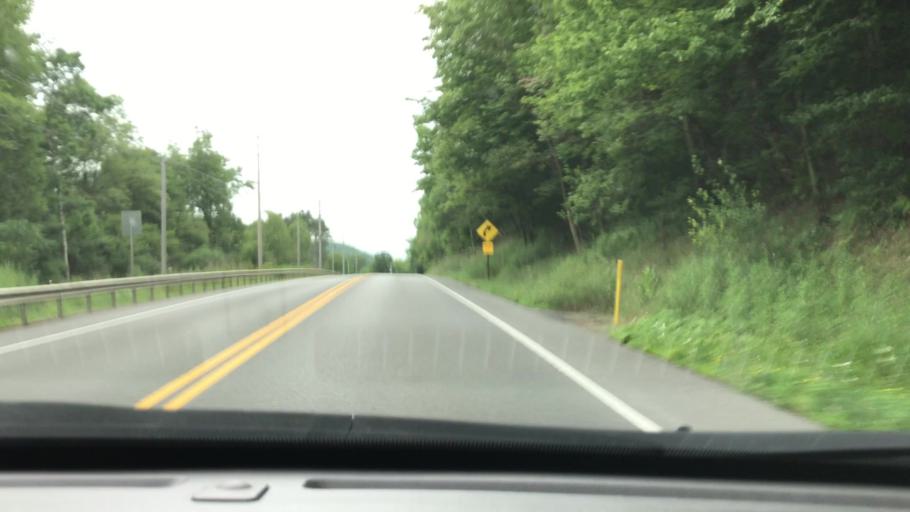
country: US
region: Pennsylvania
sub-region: Elk County
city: Johnsonburg
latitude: 41.5846
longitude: -78.6874
